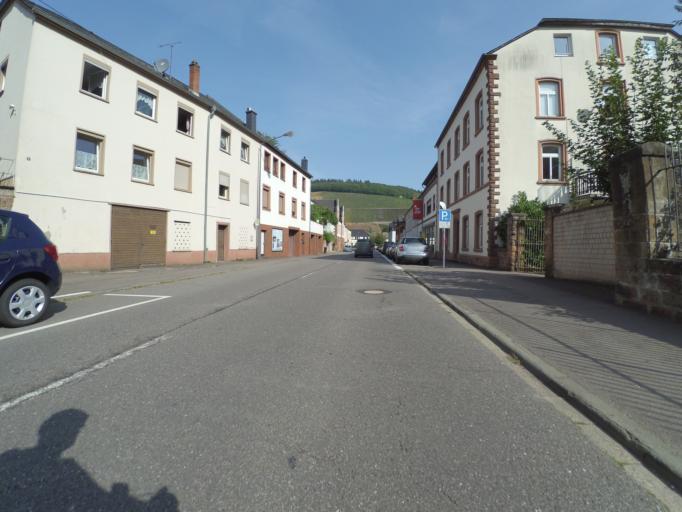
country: DE
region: Rheinland-Pfalz
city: Saarburg
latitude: 49.6104
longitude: 6.5537
